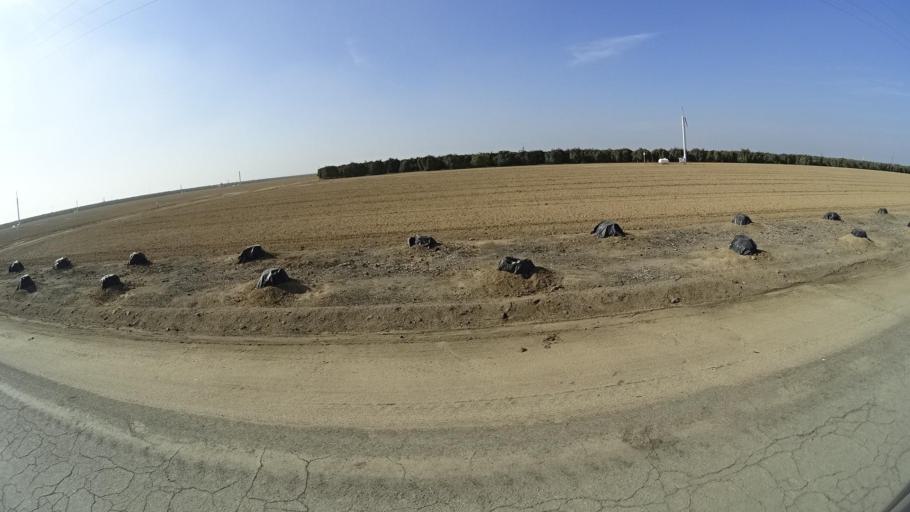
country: US
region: California
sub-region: Kern County
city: Shafter
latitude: 35.5335
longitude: -119.1336
